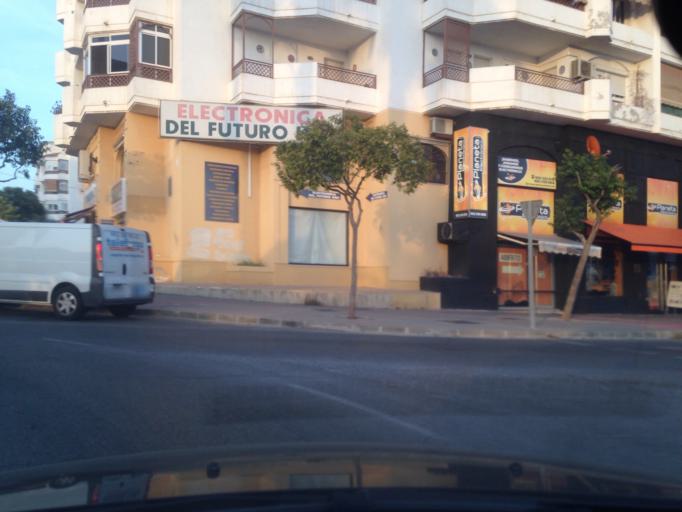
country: ES
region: Andalusia
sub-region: Provincia de Malaga
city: Malaga
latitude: 36.7165
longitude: -4.4564
